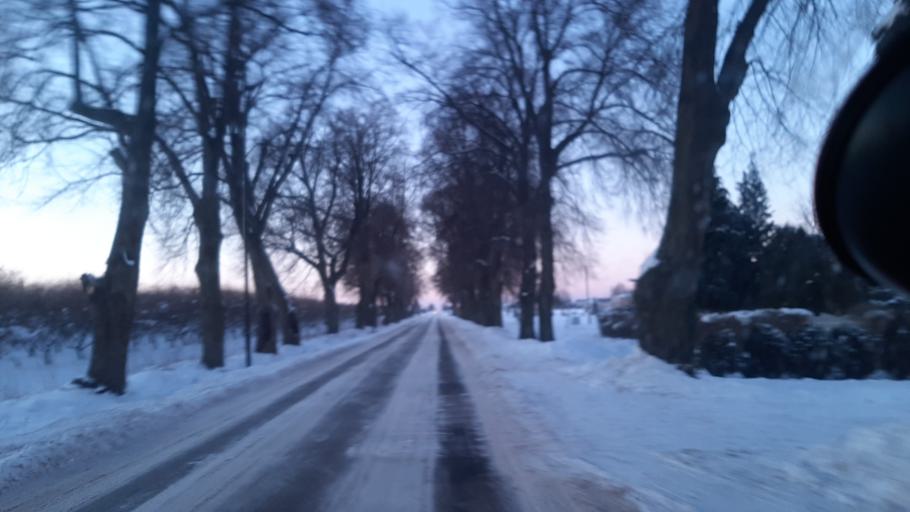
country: PL
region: Lublin Voivodeship
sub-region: Powiat lubelski
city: Lublin
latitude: 51.3344
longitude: 22.5529
